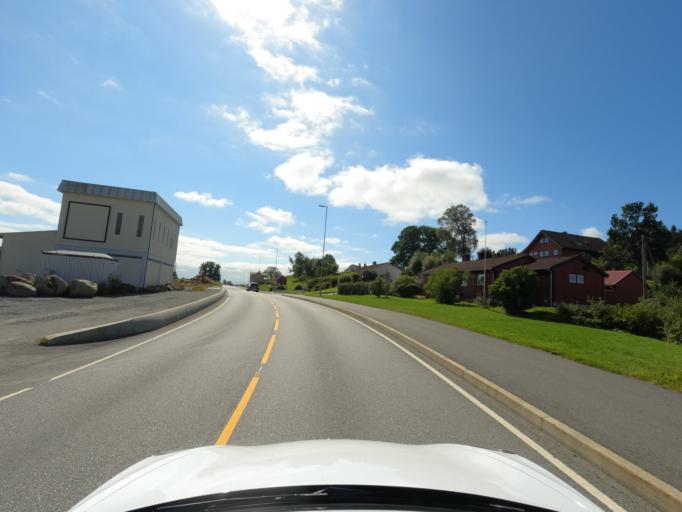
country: NO
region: Hordaland
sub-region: Os
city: Hagavik
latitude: 60.1677
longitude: 5.4200
